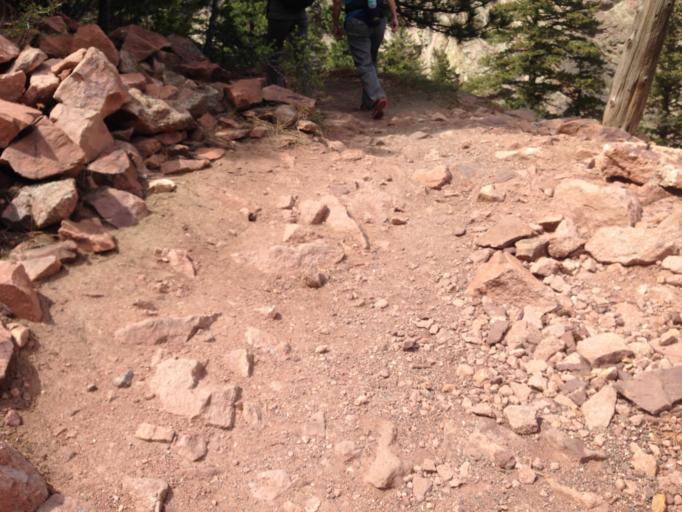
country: US
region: Colorado
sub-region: Boulder County
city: Boulder
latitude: 39.9302
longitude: -105.2815
